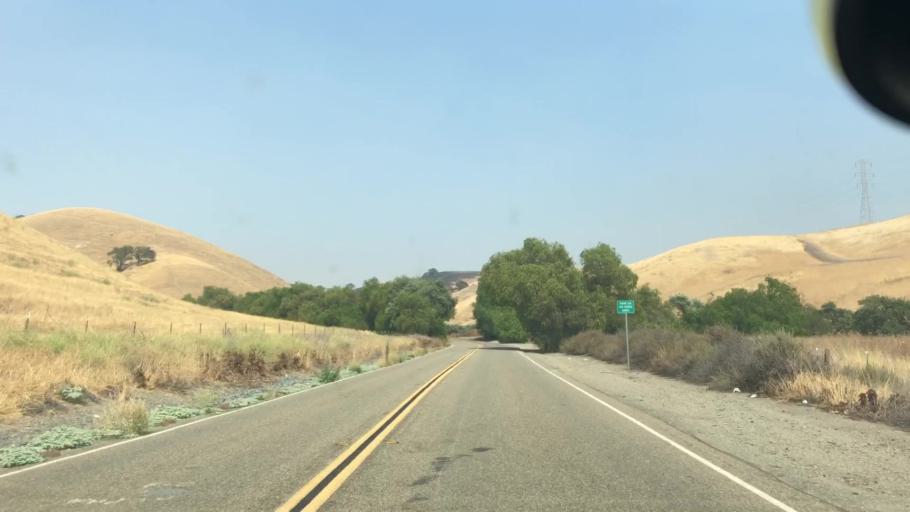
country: US
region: California
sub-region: Alameda County
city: Livermore
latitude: 37.6458
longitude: -121.6276
